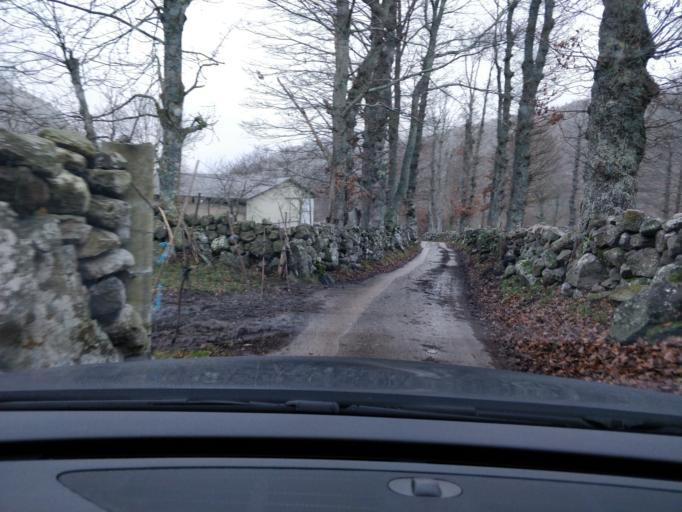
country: ES
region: Castille and Leon
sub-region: Provincia de Burgos
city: Espinosa de los Monteros
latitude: 43.1287
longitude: -3.6124
